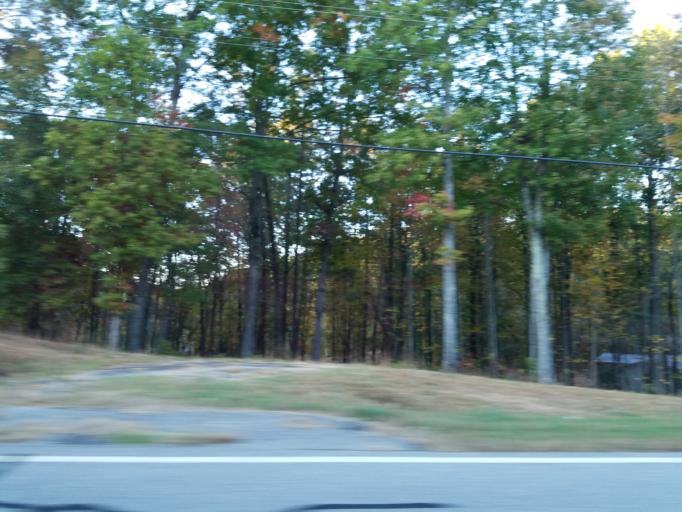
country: US
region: Georgia
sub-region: Lumpkin County
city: Dahlonega
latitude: 34.5493
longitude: -84.0983
